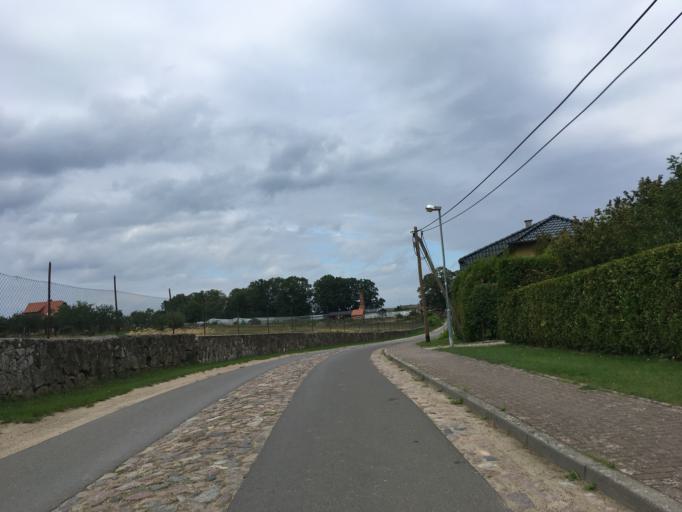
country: DE
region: Brandenburg
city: Joachimsthal
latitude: 53.0221
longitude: 13.7601
